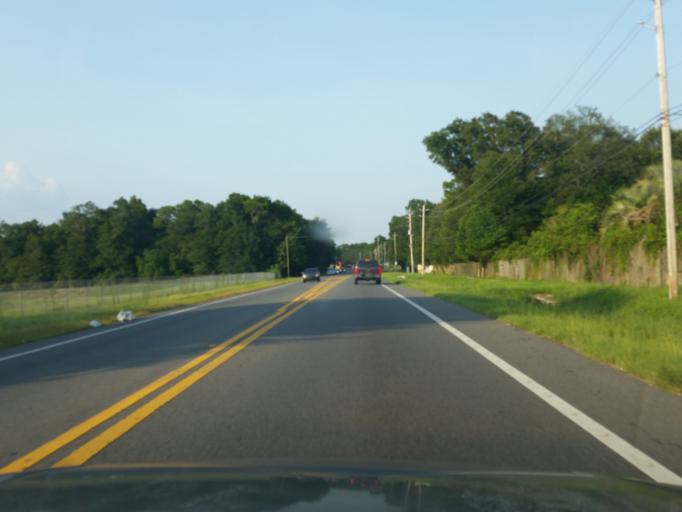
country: US
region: Florida
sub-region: Escambia County
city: Ferry Pass
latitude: 30.5144
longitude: -87.1803
